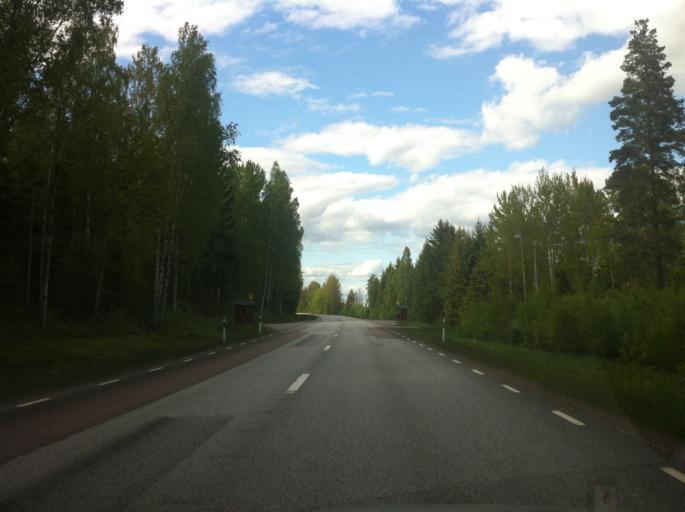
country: SE
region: Vaermland
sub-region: Storfors Kommun
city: Storfors
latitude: 59.4787
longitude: 14.2586
